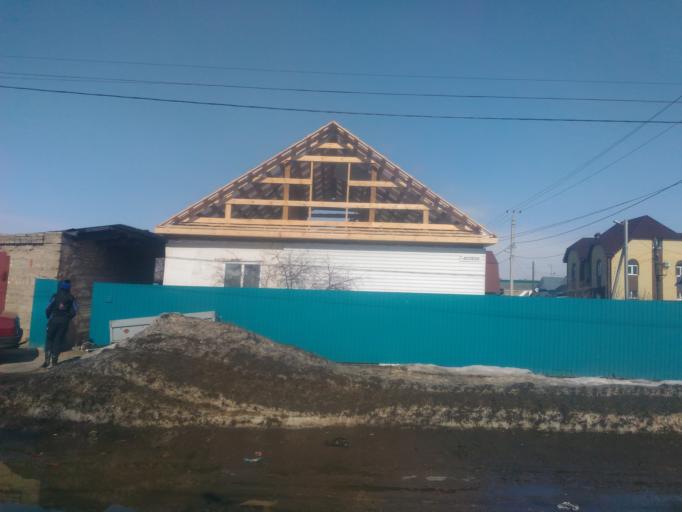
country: RU
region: Ulyanovsk
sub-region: Ulyanovskiy Rayon
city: Ulyanovsk
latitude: 54.3506
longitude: 48.5456
